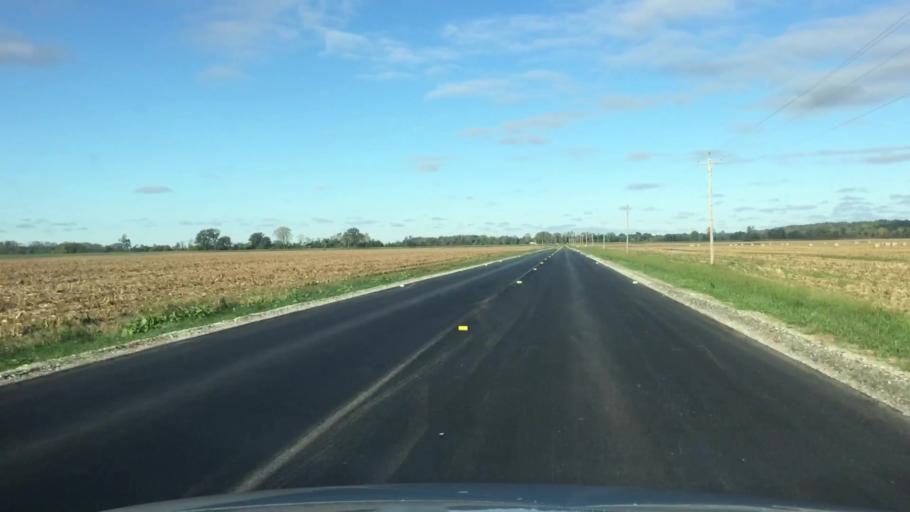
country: US
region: Missouri
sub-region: Howard County
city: New Franklin
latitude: 39.0013
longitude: -92.6838
